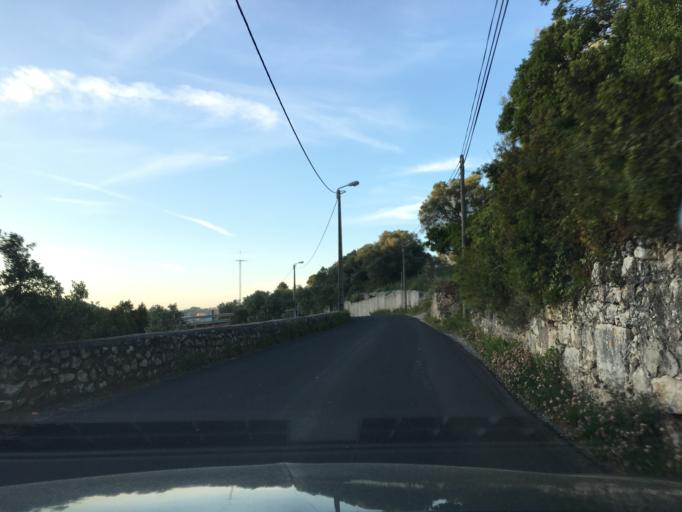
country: PT
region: Lisbon
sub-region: Oeiras
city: Quejas
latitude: 38.7182
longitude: -9.2760
